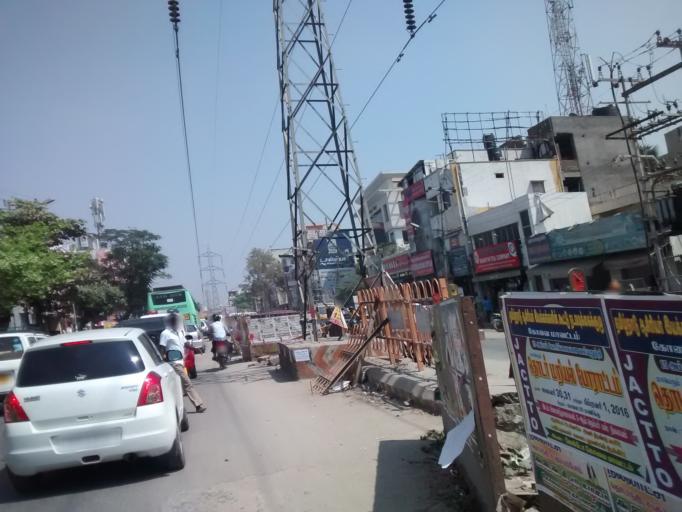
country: IN
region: Tamil Nadu
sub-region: Coimbatore
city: Coimbatore
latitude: 11.0203
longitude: 76.9679
